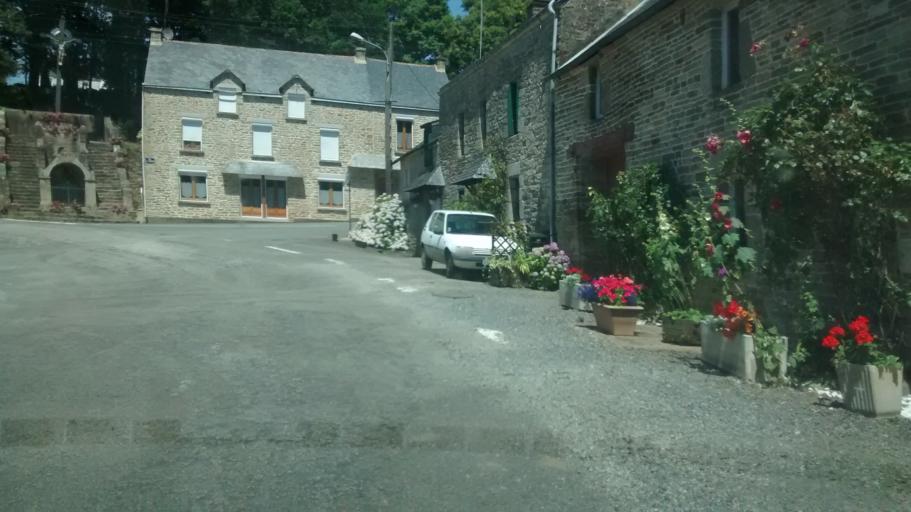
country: FR
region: Brittany
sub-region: Departement du Morbihan
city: Molac
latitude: 47.7303
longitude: -2.4378
